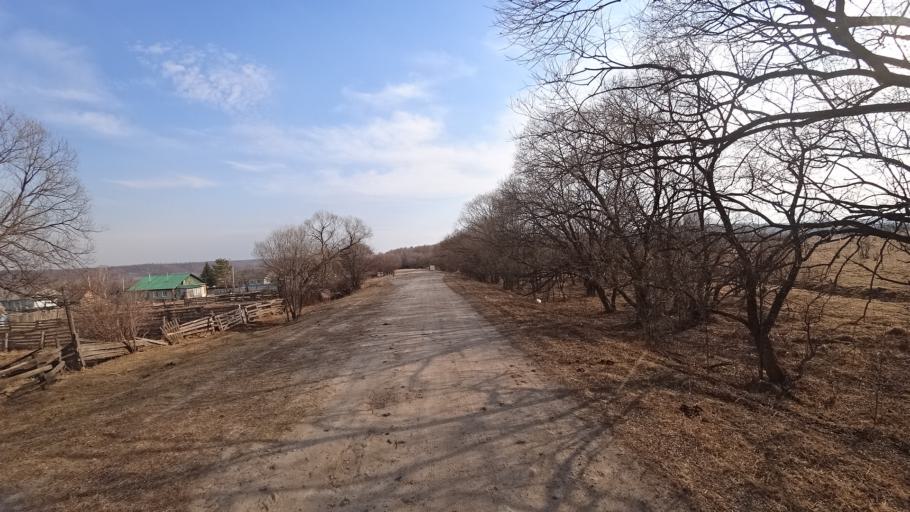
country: RU
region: Amur
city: Novobureyskiy
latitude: 49.8976
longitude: 129.8743
